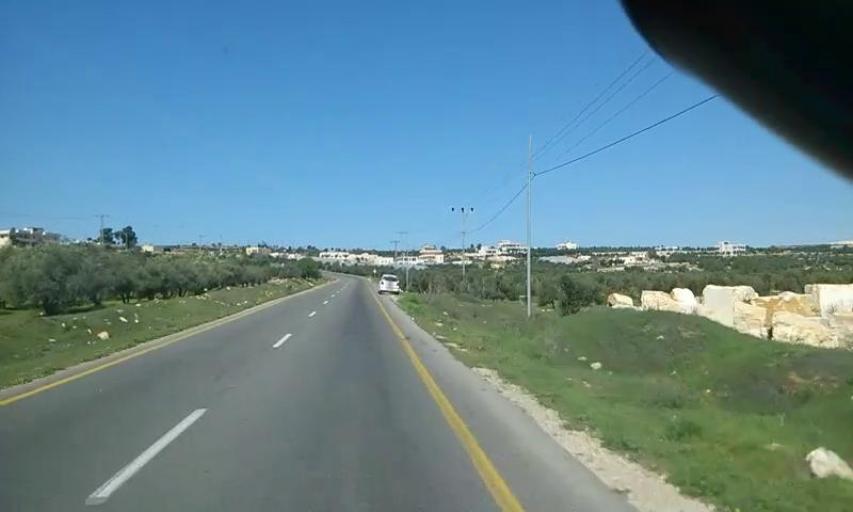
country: PS
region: West Bank
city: Marah Rabbah
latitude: 31.6434
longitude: 35.1950
